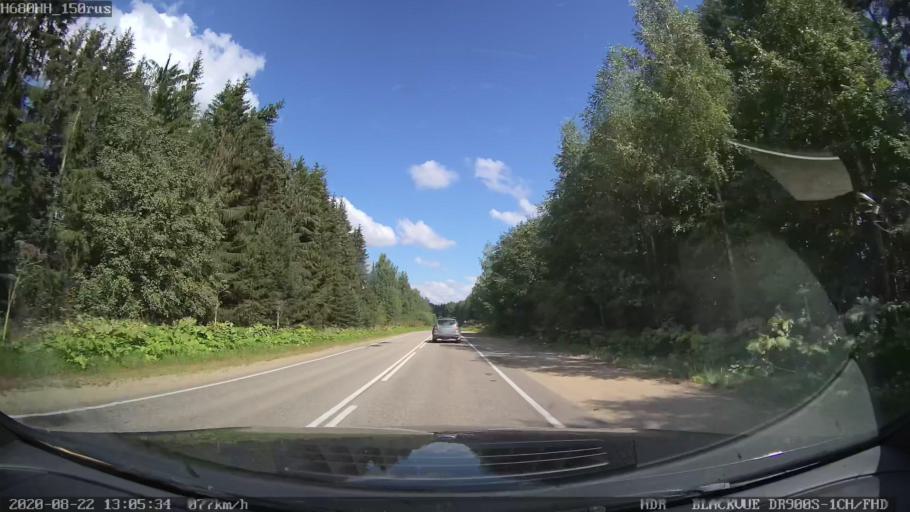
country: RU
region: Tverskaya
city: Bezhetsk
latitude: 57.6732
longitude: 36.4490
